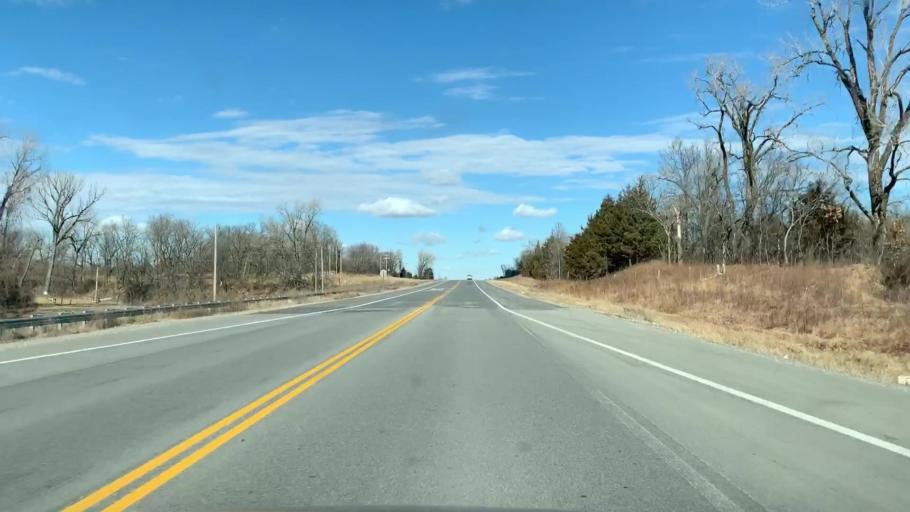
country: US
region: Kansas
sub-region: Cherokee County
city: Columbus
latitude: 37.3221
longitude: -94.8323
